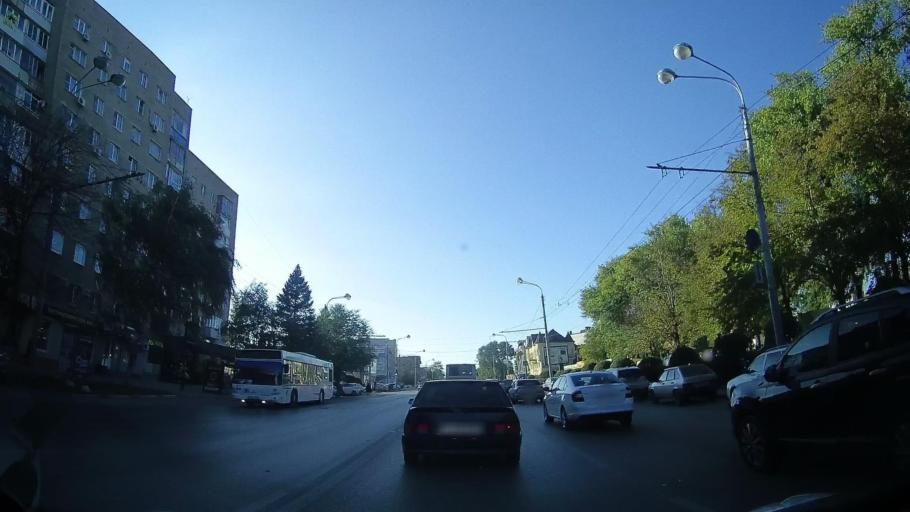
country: RU
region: Rostov
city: Rostov-na-Donu
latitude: 47.2113
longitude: 39.6678
